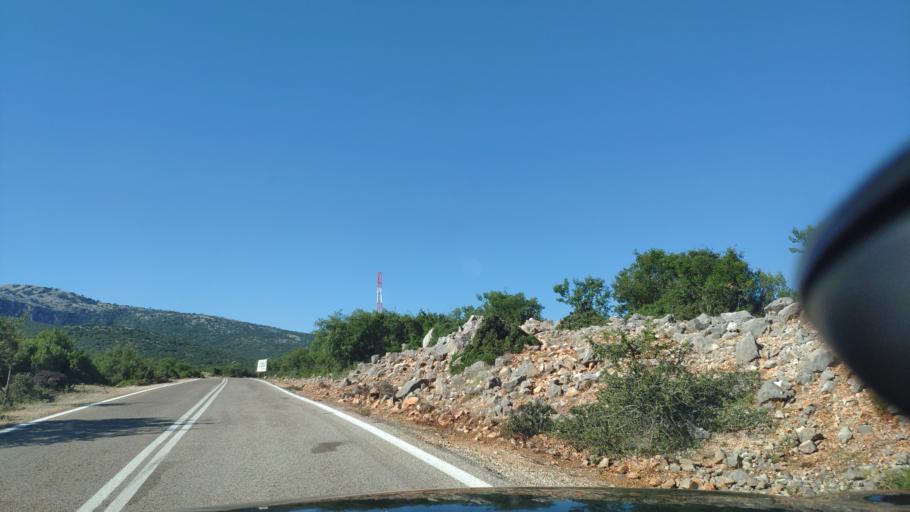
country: GR
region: West Greece
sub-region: Nomos Aitolias kai Akarnanias
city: Archontochorion
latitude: 38.6934
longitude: 21.0763
